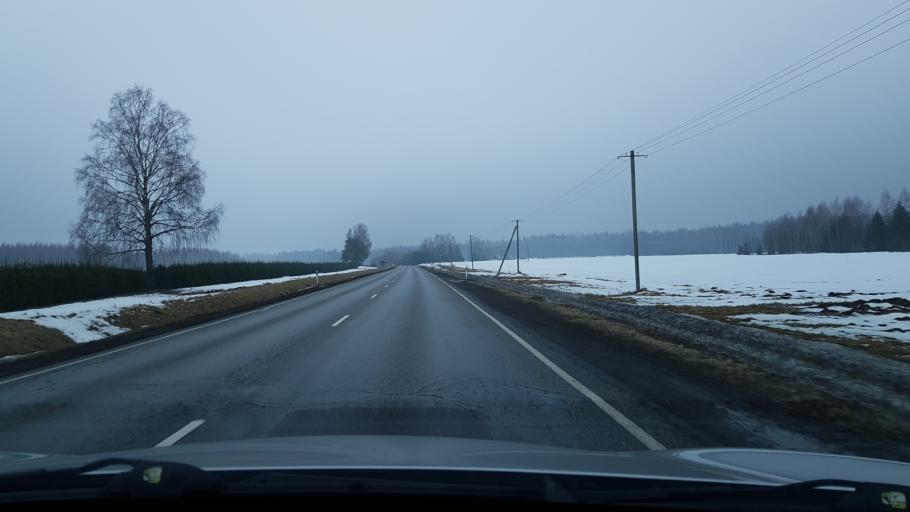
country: EE
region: Valgamaa
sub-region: Valga linn
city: Valga
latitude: 57.9023
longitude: 26.1720
